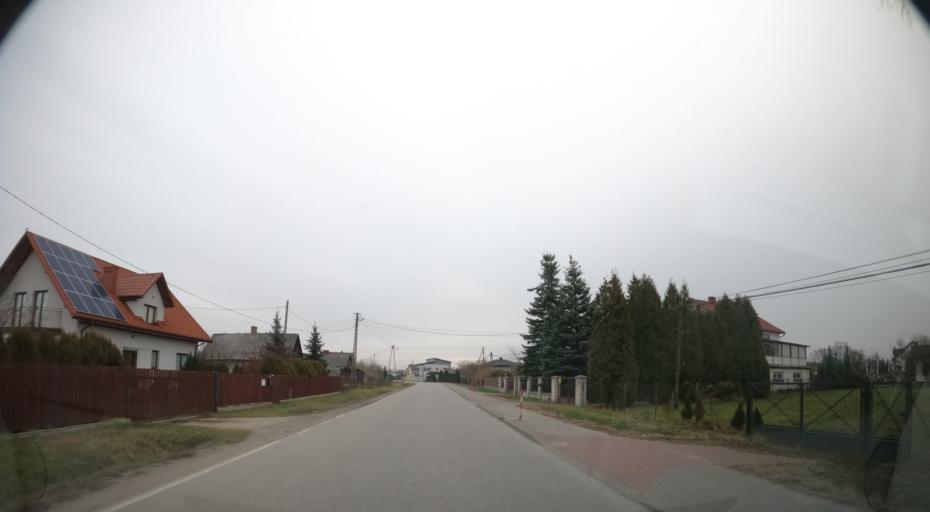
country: PL
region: Masovian Voivodeship
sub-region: Powiat radomski
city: Jedlinsk
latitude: 51.4868
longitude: 21.1291
